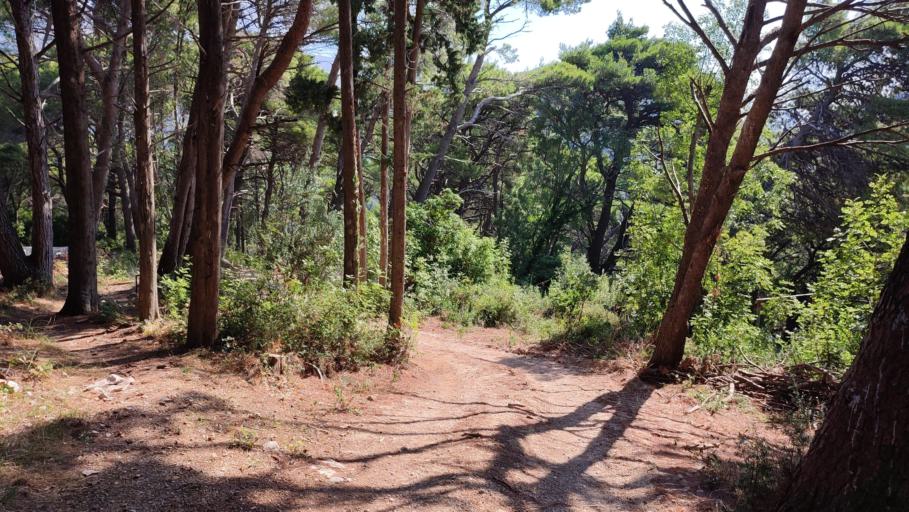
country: ME
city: Petrovac na Moru
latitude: 42.2014
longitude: 18.9484
